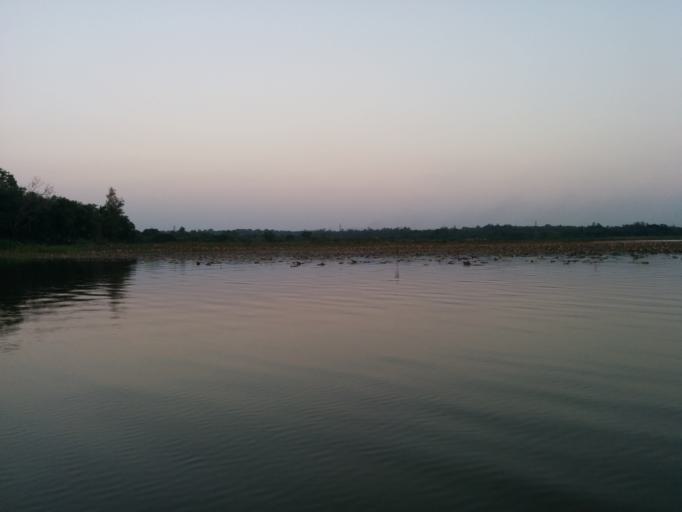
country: IN
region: Tamil Nadu
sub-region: Villupuram
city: Auroville
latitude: 11.9551
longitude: 79.7519
